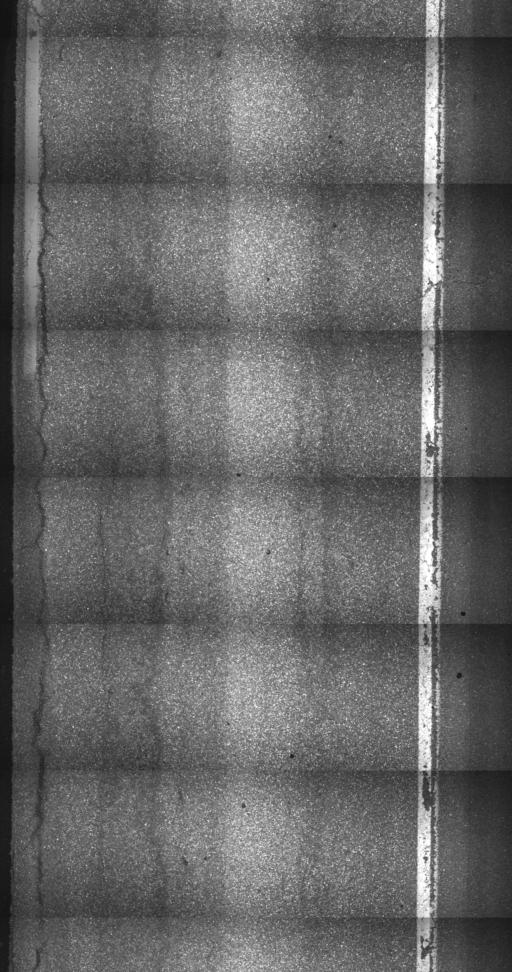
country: US
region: Vermont
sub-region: Chittenden County
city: Jericho
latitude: 44.5472
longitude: -72.9469
